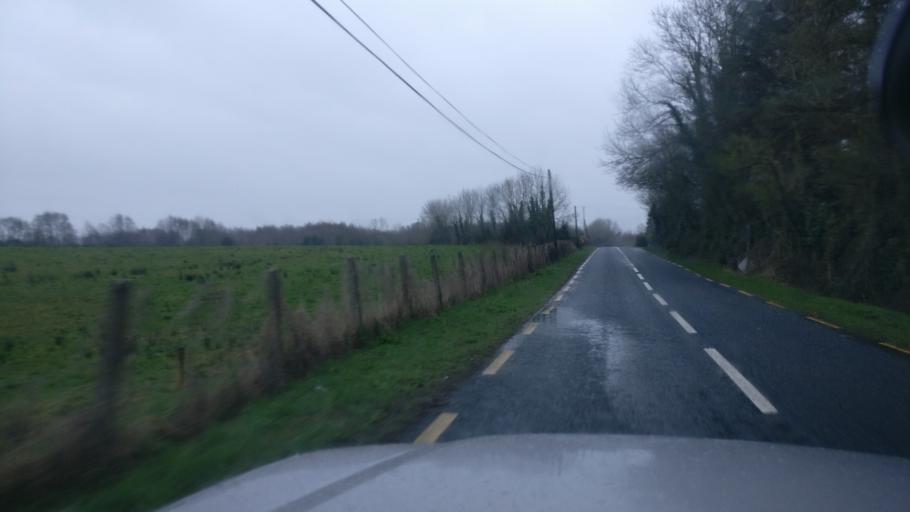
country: IE
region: Connaught
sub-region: County Galway
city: Ballinasloe
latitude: 53.2200
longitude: -8.1948
